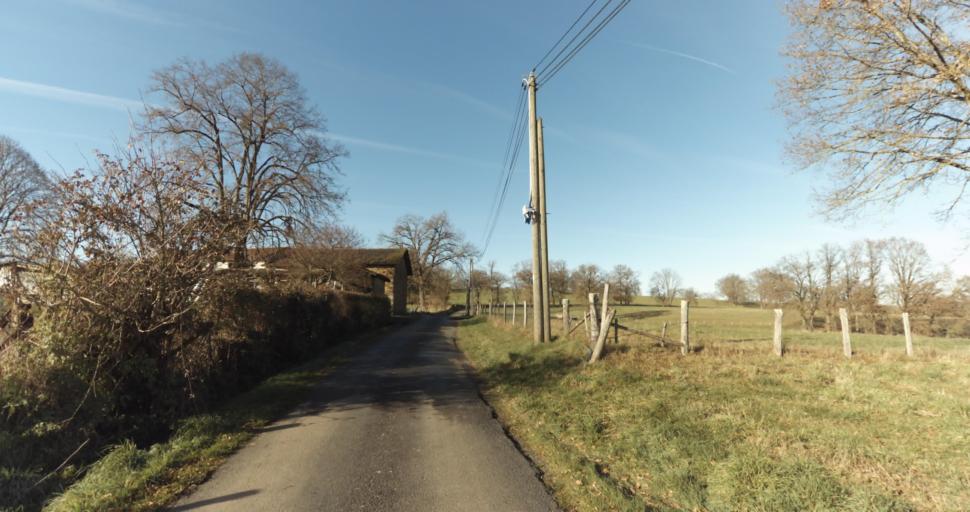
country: FR
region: Limousin
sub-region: Departement de la Haute-Vienne
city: Saint-Priest-sous-Aixe
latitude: 45.7929
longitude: 1.1098
